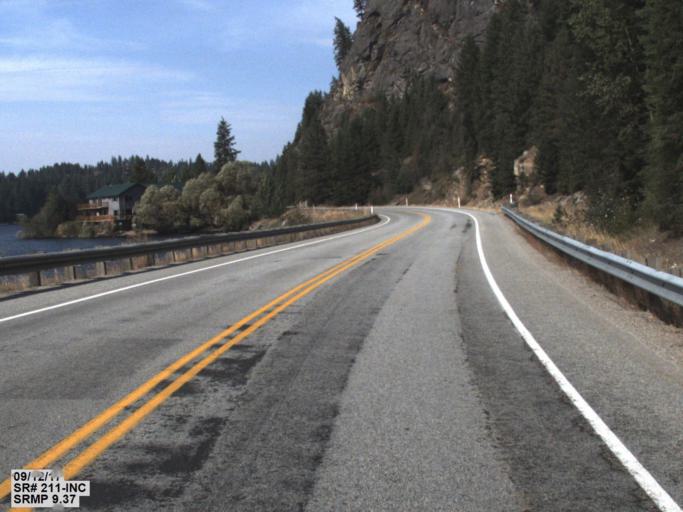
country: US
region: Washington
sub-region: Pend Oreille County
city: Newport
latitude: 48.2228
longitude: -117.2916
